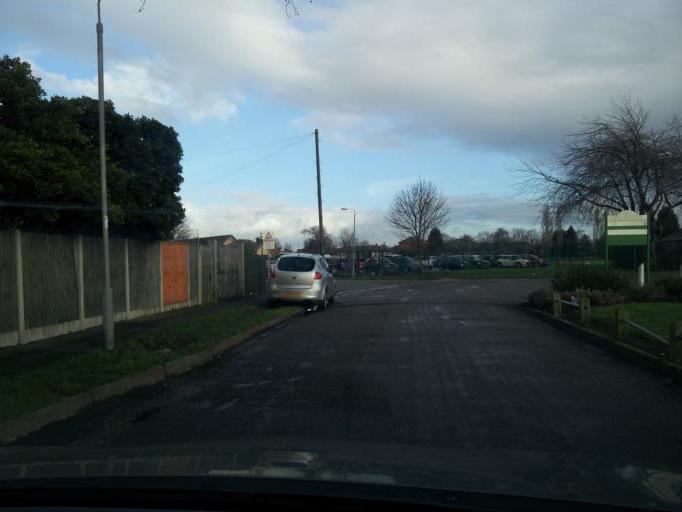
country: GB
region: England
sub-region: Nottinghamshire
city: Newark on Trent
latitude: 53.0658
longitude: -0.8105
